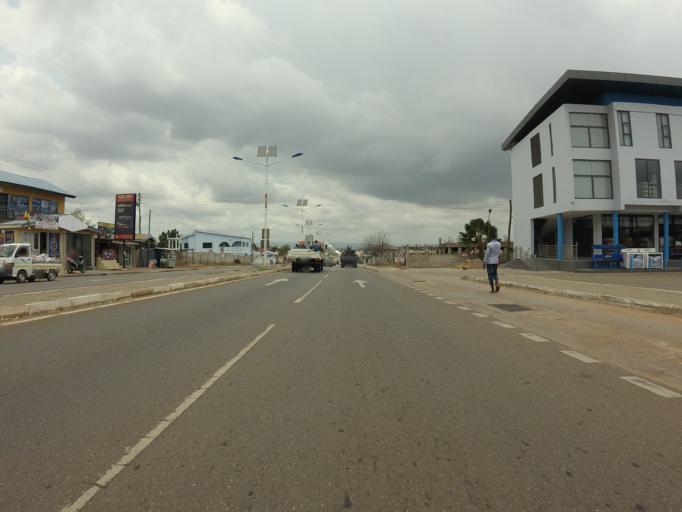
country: GH
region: Greater Accra
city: Medina Estates
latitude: 5.6700
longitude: -0.1515
